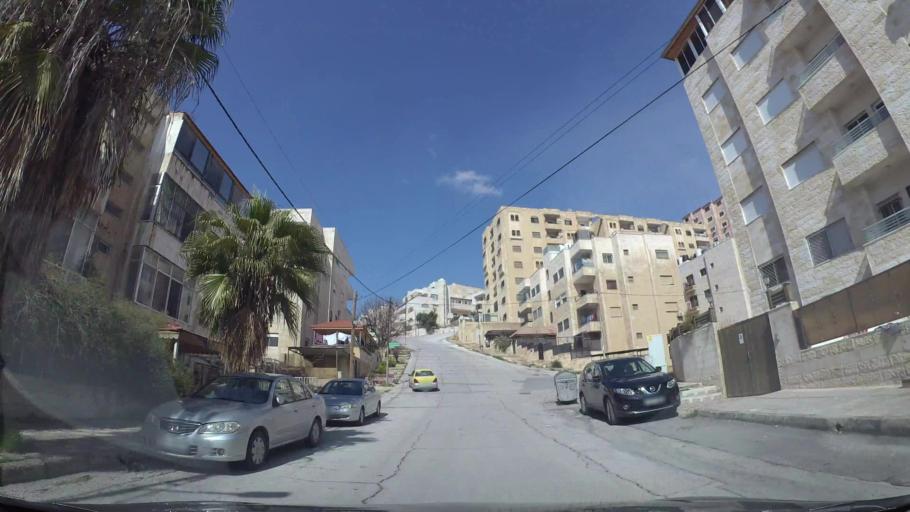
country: JO
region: Amman
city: Al Jubayhah
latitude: 31.9895
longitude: 35.8999
